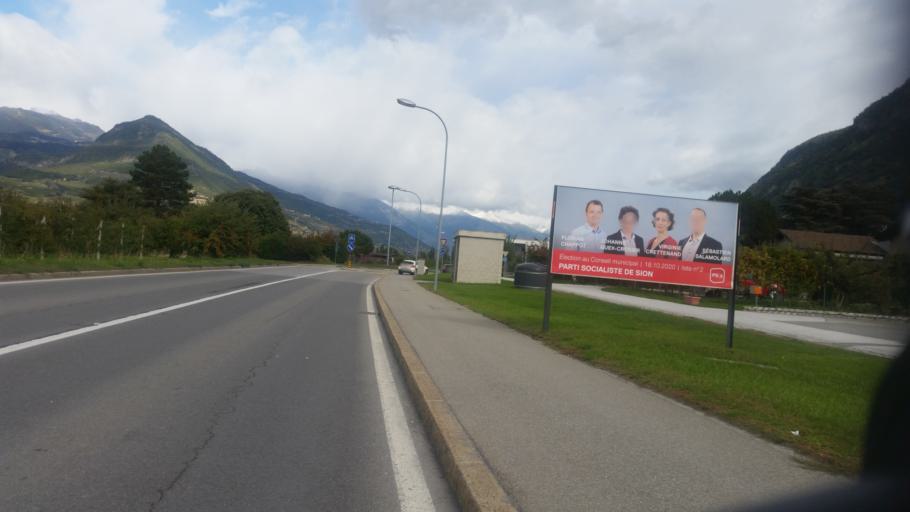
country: CH
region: Valais
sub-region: Sion District
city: Saint-Leonard
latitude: 46.2360
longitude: 7.3997
